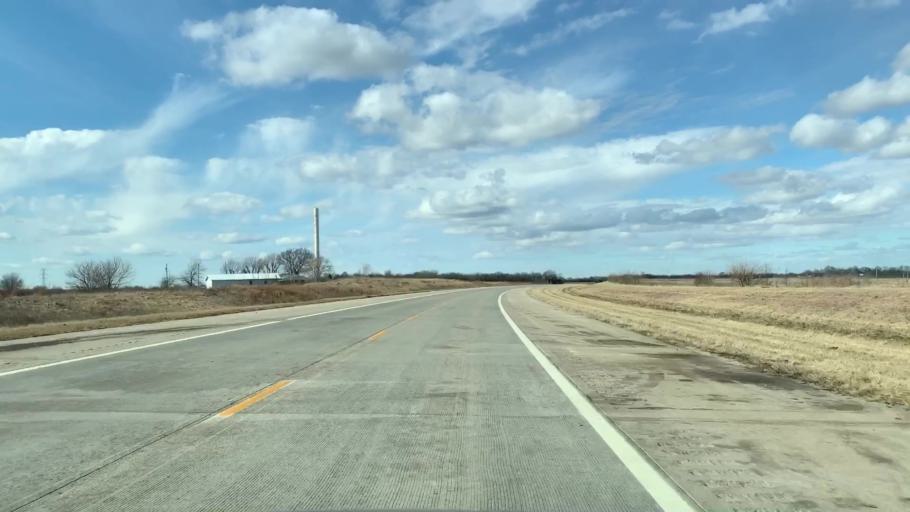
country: US
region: Kansas
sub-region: Labette County
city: Parsons
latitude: 37.3526
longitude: -95.2092
